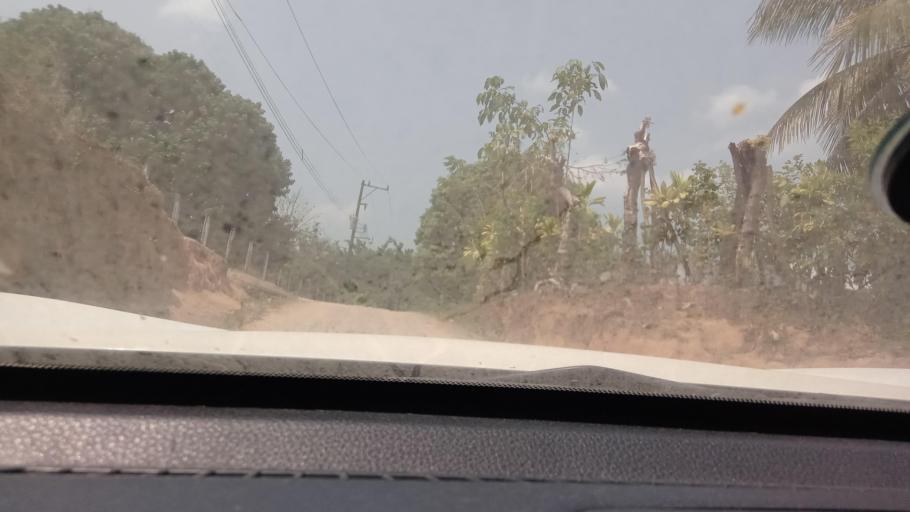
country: MX
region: Chiapas
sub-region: Tecpatan
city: Raudales Malpaso
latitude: 17.4736
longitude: -93.8227
